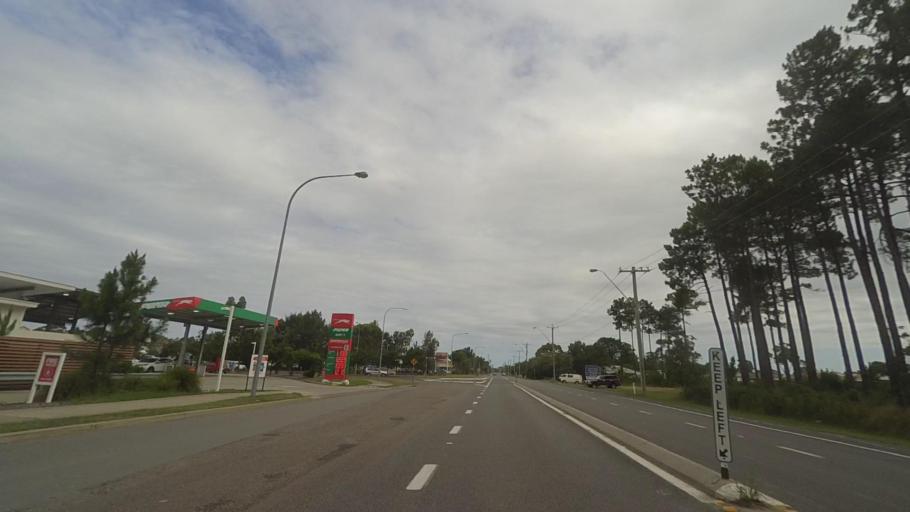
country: AU
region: New South Wales
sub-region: Great Lakes
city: Hawks Nest
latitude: -32.6508
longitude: 152.1487
